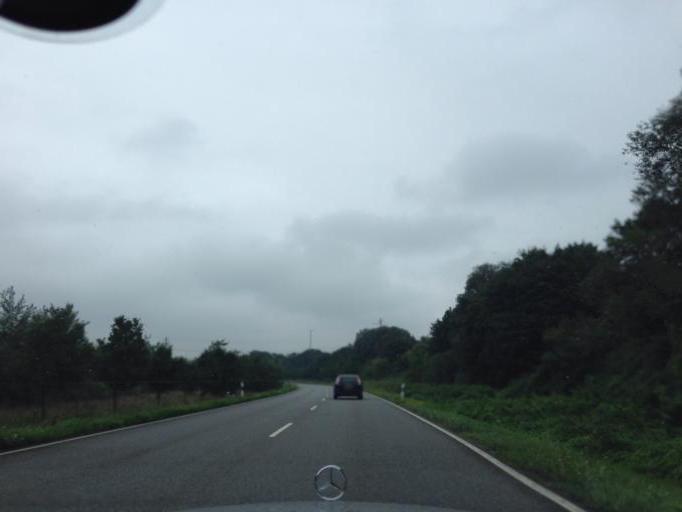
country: DE
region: Schleswig-Holstein
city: Barsbuettel
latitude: 53.5627
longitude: 10.1729
